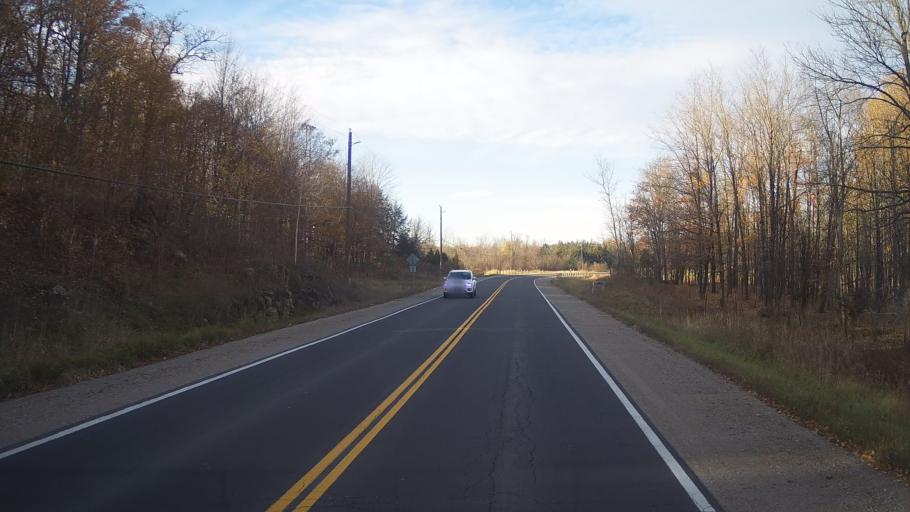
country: CA
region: Ontario
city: Perth
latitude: 44.8209
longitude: -76.3176
